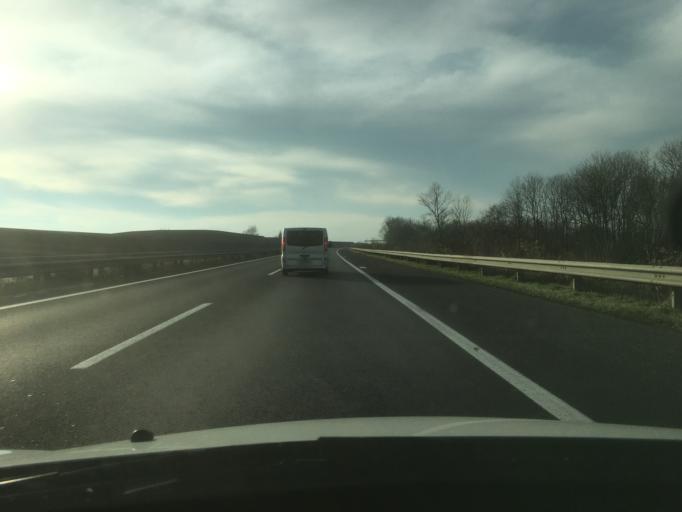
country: AT
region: Upper Austria
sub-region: Politischer Bezirk Linz-Land
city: Horsching
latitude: 48.1941
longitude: 14.1856
